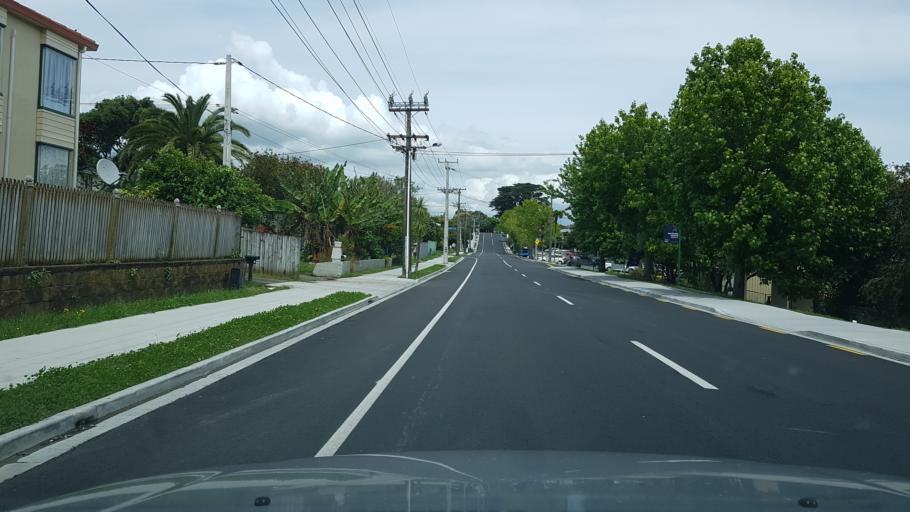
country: NZ
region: Auckland
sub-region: Auckland
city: North Shore
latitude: -36.8010
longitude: 174.7482
